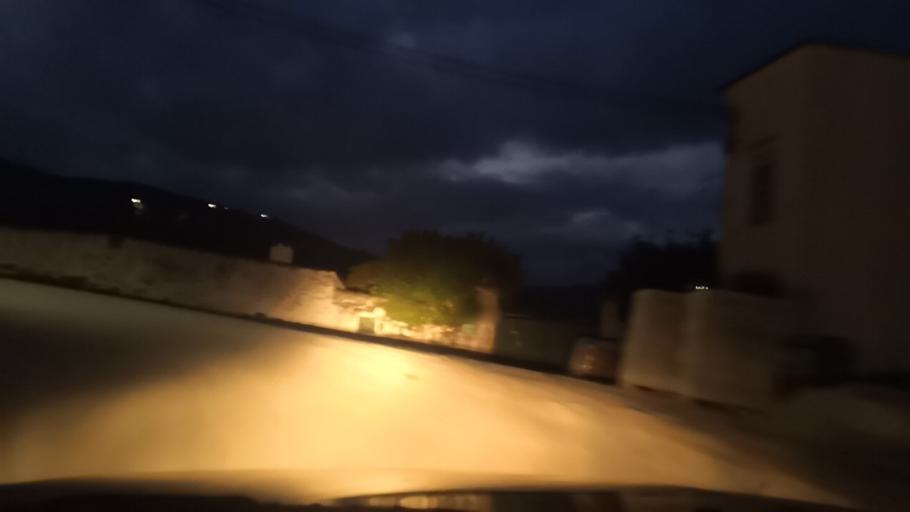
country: PT
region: Viseu
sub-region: Tabuaco
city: Tabuaco
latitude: 41.1593
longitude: -7.5224
